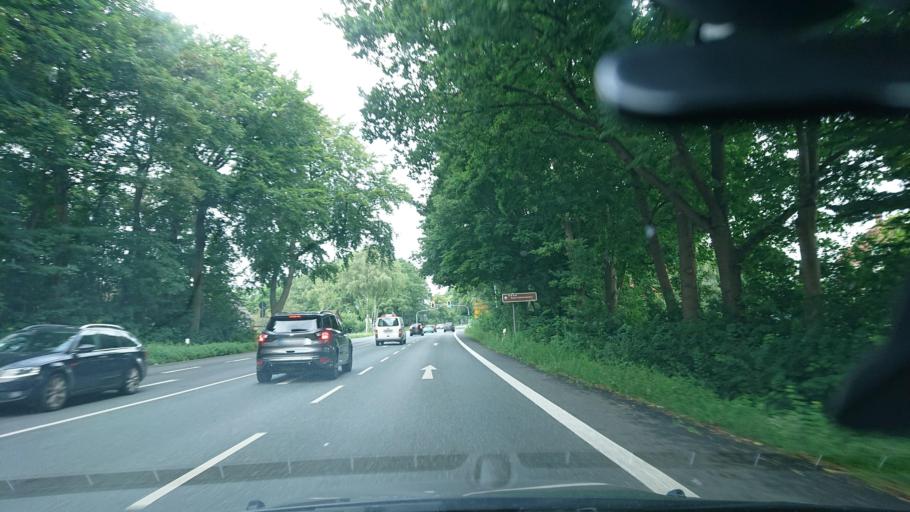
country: DE
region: North Rhine-Westphalia
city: Werne
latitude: 51.6519
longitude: 7.6751
